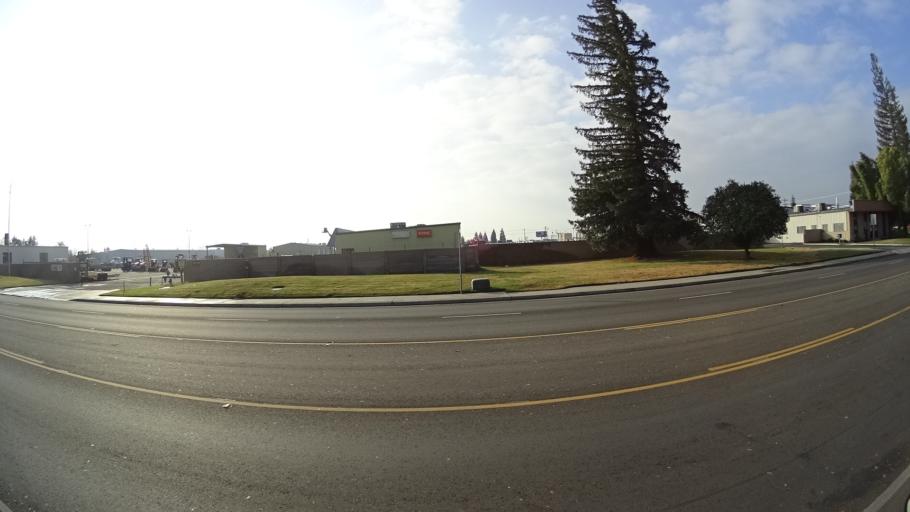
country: US
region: California
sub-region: Kern County
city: Greenacres
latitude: 35.3132
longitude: -119.0735
